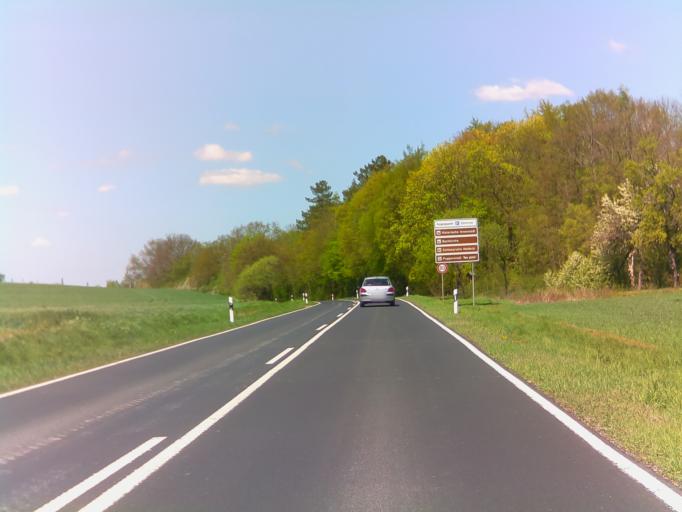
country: DE
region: Thuringia
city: Dornheim
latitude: 50.8112
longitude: 10.9756
